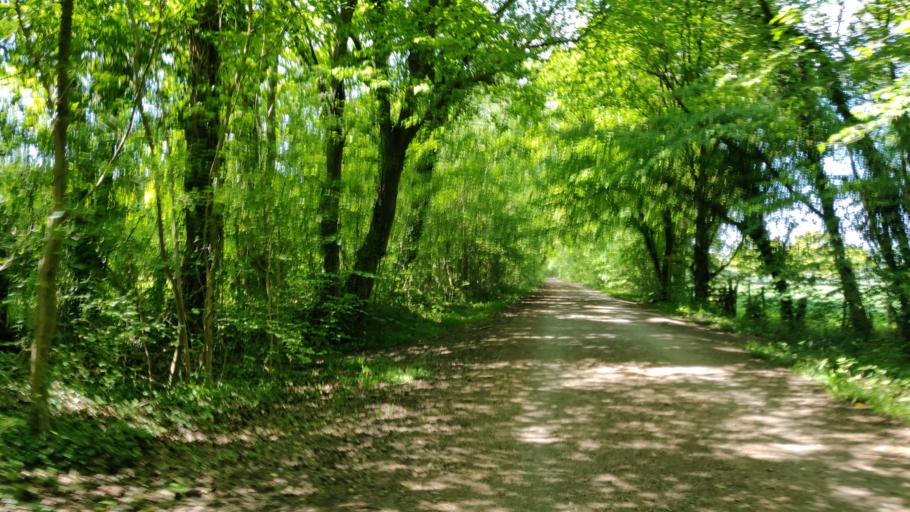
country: GB
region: England
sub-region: West Sussex
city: Rudgwick
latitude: 51.0756
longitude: -0.4282
